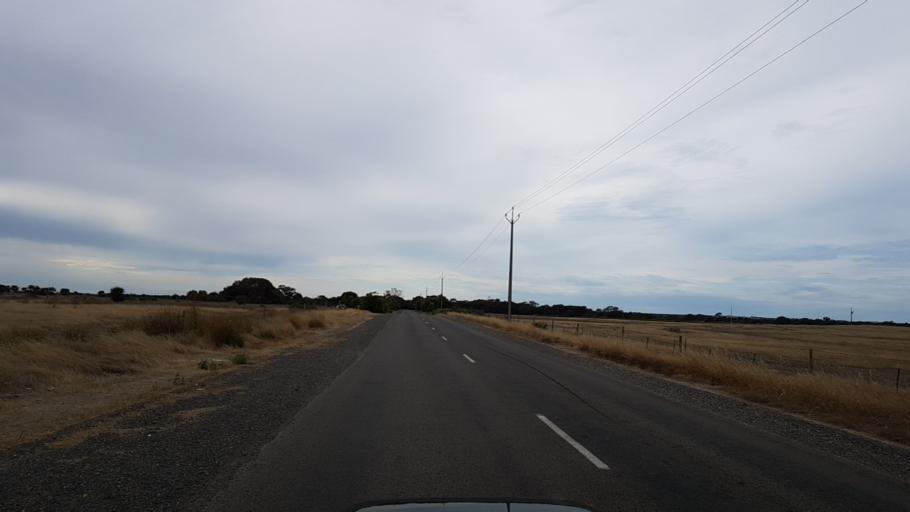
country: AU
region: South Australia
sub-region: Yorke Peninsula
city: Port Victoria
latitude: -34.9207
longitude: 137.0722
